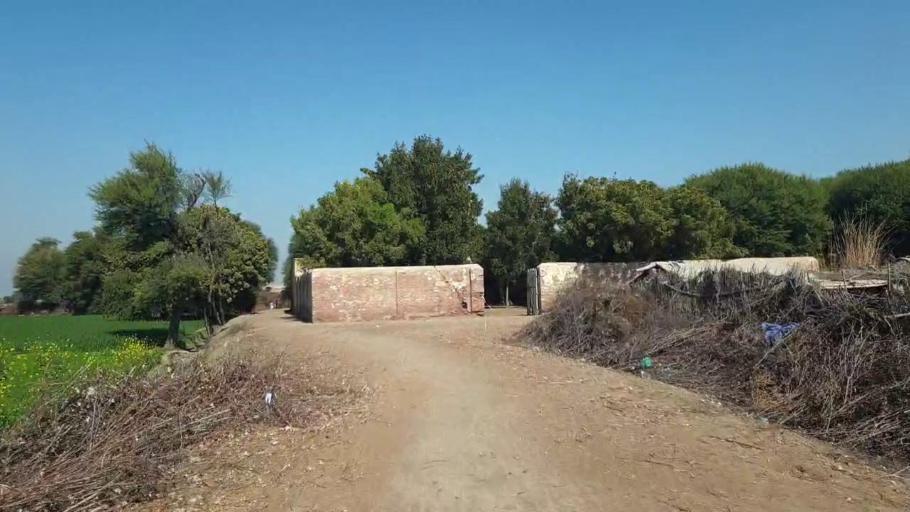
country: PK
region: Sindh
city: Shahpur Chakar
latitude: 26.1239
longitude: 68.6459
